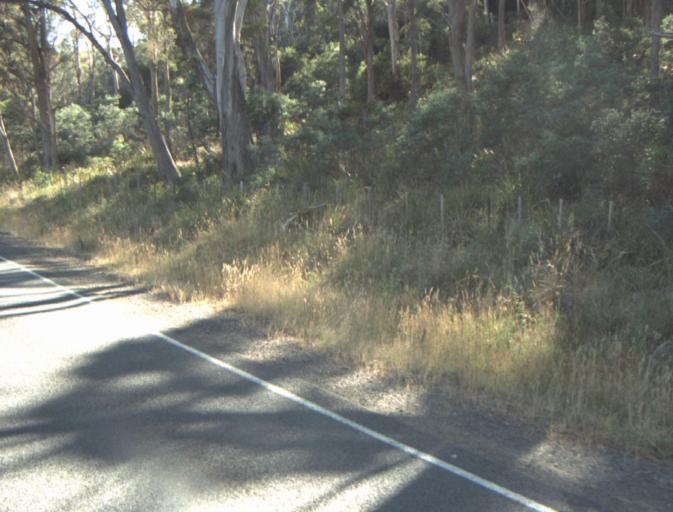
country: AU
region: Tasmania
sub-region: Launceston
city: Newstead
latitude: -41.4211
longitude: 147.2563
